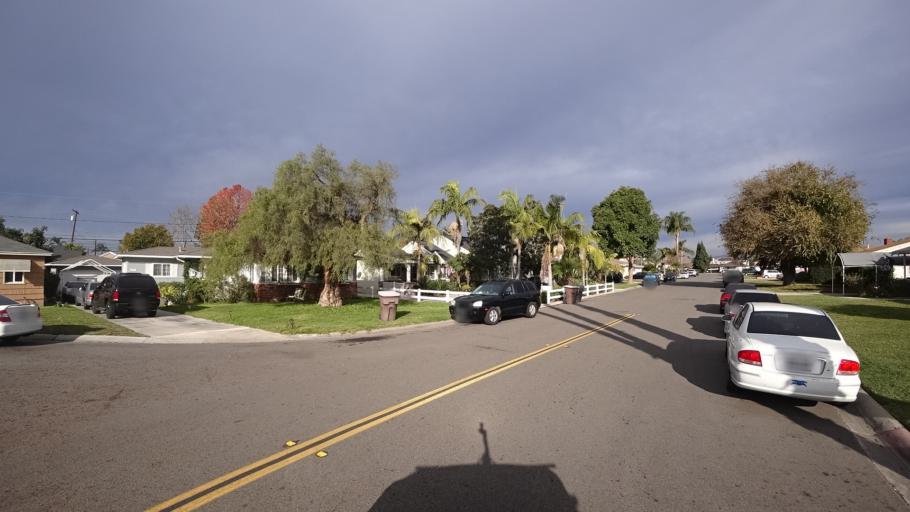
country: US
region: California
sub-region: Orange County
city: Garden Grove
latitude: 33.7752
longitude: -117.9312
